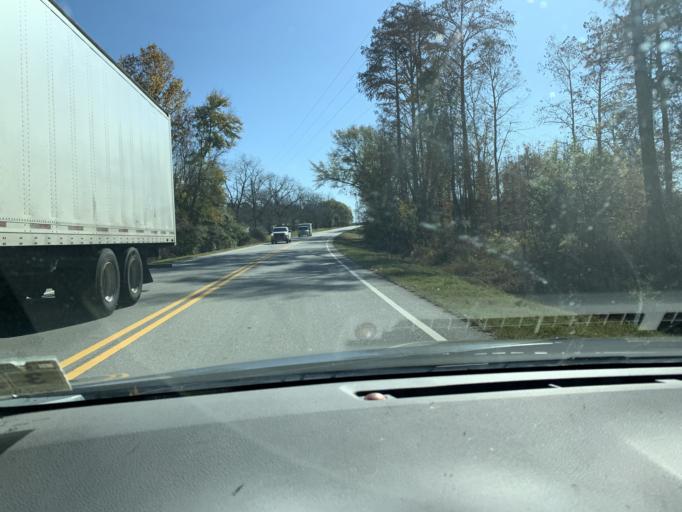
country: US
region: Georgia
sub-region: Ben Hill County
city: Fitzgerald
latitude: 31.7124
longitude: -83.1700
